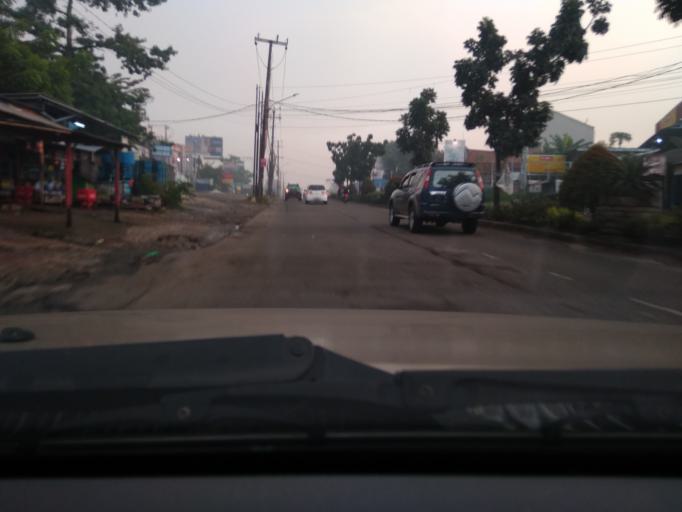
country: ID
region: West Java
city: Serpong
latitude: -6.3271
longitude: 106.6844
